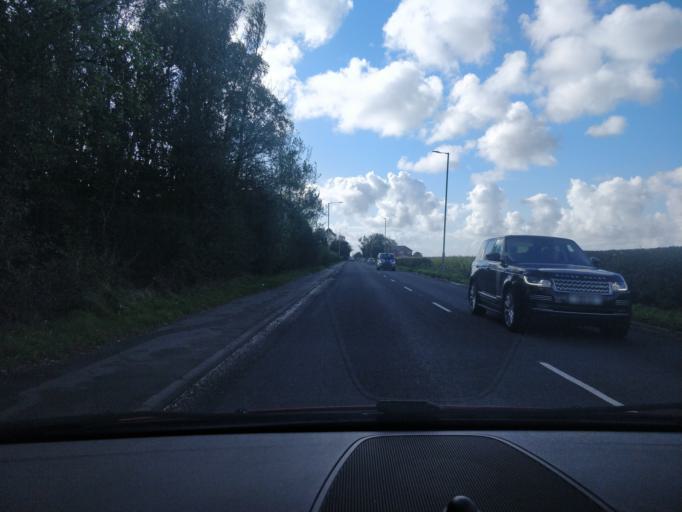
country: GB
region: England
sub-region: Lancashire
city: Ormskirk
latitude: 53.5856
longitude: -2.8660
